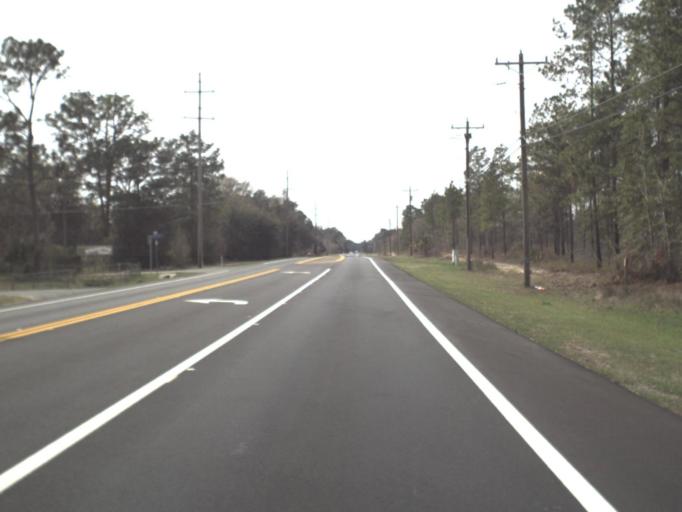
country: US
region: Florida
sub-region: Gadsden County
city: Midway
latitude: 30.4416
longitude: -84.4361
